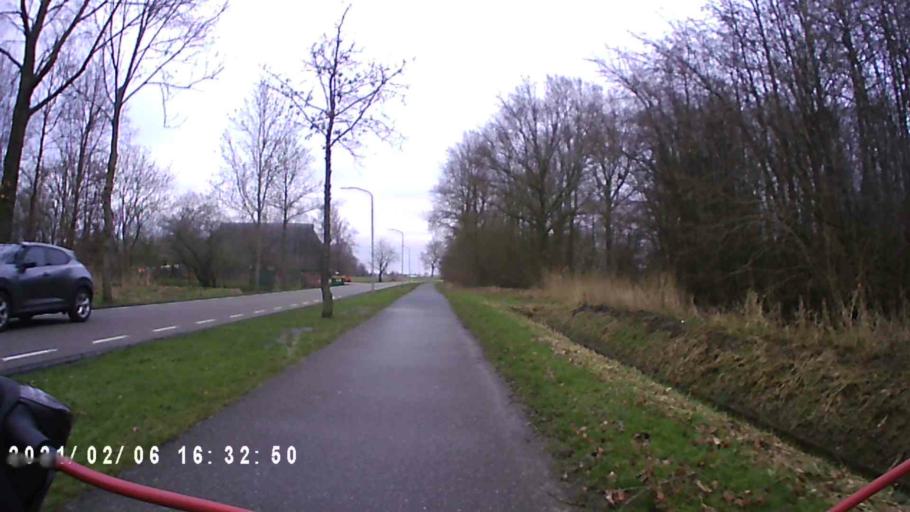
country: NL
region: Groningen
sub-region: Gemeente Bedum
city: Bedum
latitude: 53.4112
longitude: 6.6916
